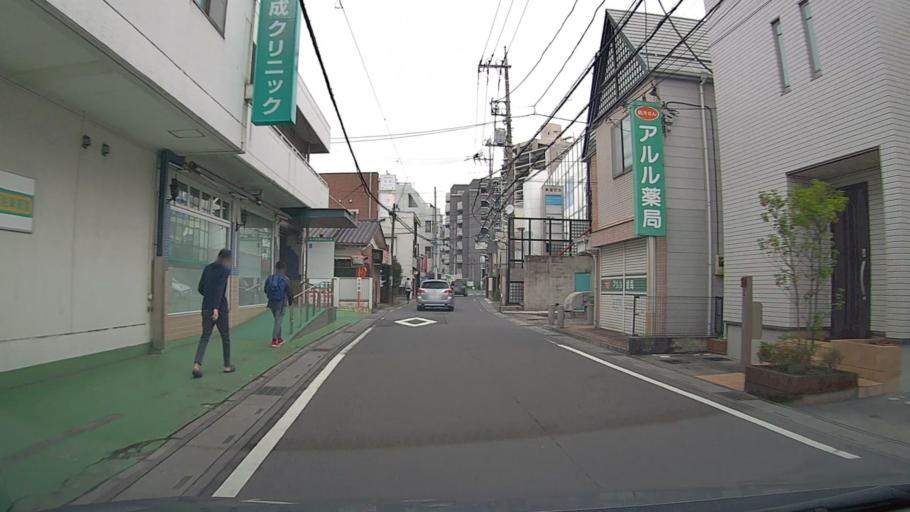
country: JP
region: Saitama
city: Tokorozawa
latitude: 35.7841
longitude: 139.4751
